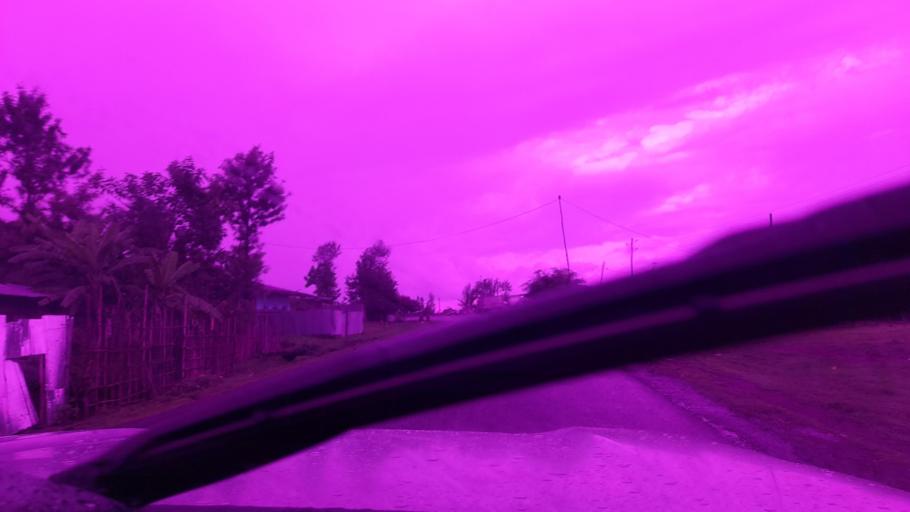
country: ET
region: Oromiya
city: Jima
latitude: 7.7146
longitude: 37.0975
